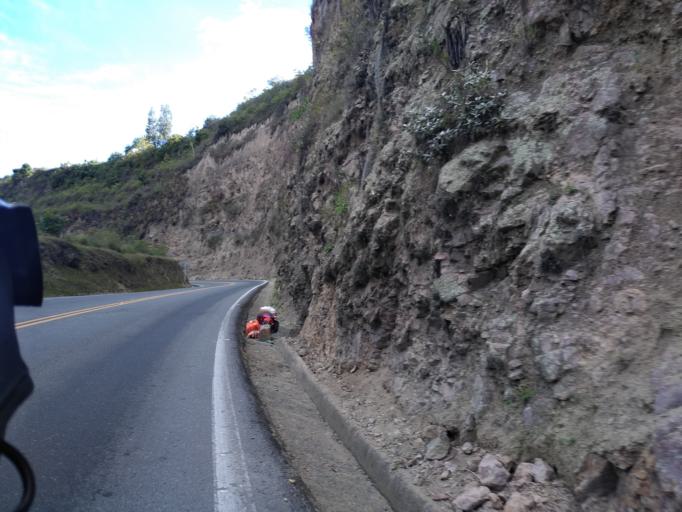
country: CO
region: Narino
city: Imues
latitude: 1.0548
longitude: -77.4500
